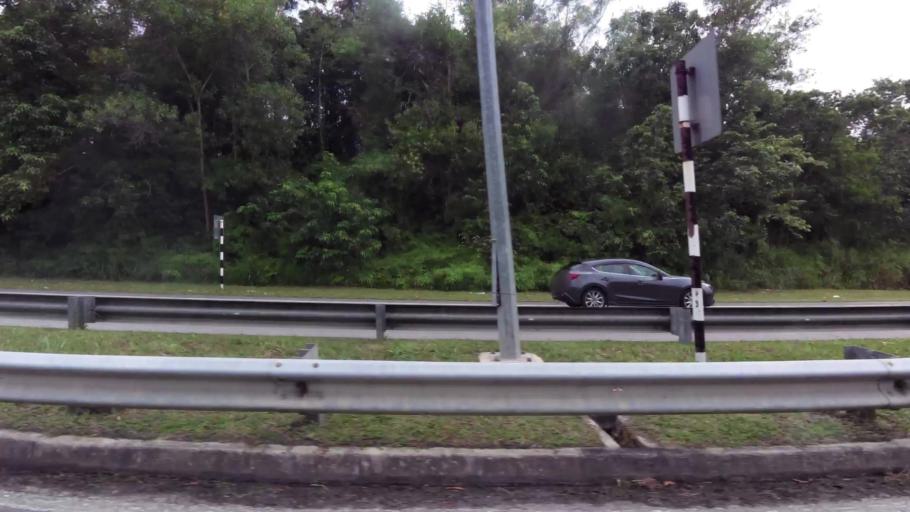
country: BN
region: Brunei and Muara
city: Bandar Seri Begawan
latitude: 4.9103
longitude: 114.9079
